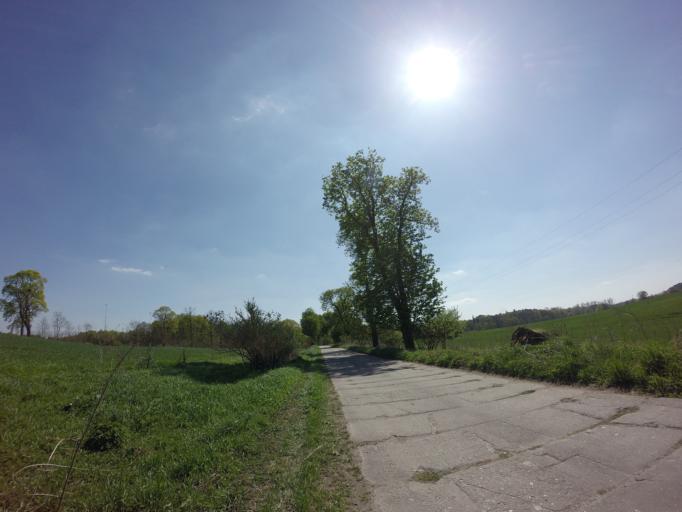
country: PL
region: West Pomeranian Voivodeship
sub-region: Powiat stargardzki
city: Suchan
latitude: 53.1847
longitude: 15.3197
